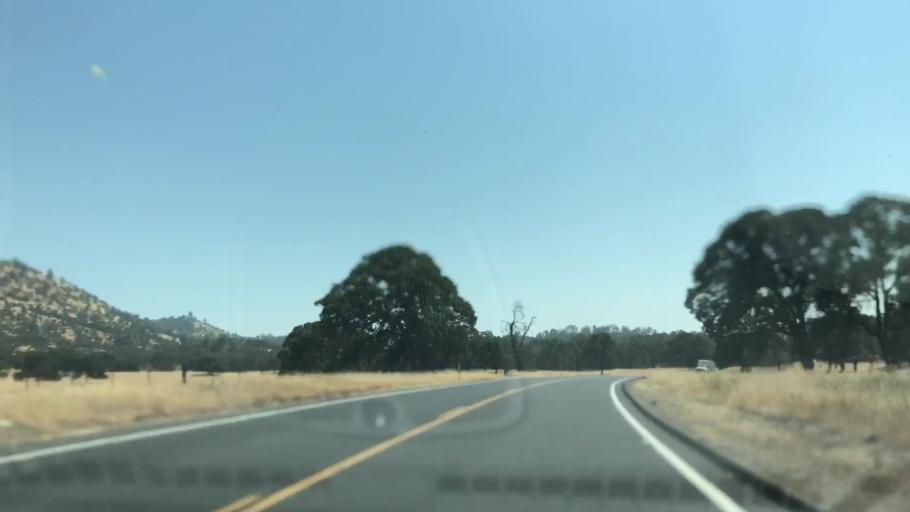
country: US
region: California
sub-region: Calaveras County
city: Copperopolis
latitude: 37.9596
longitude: -120.6141
